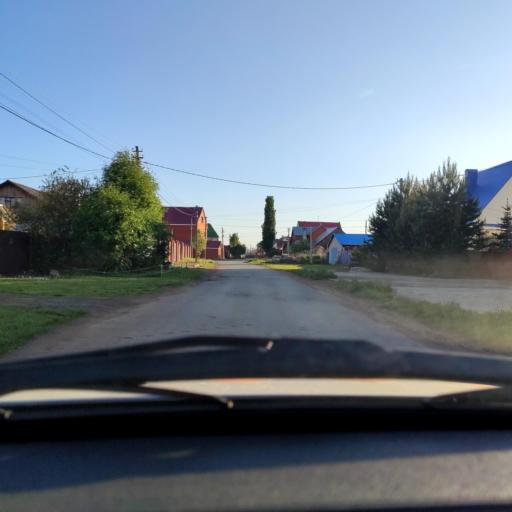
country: RU
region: Bashkortostan
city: Ufa
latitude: 54.8398
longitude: 56.0054
